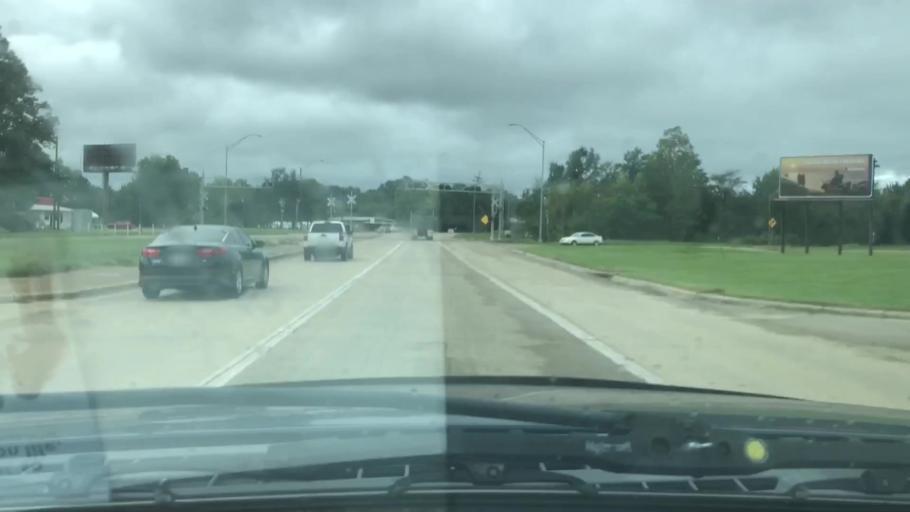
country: US
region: Texas
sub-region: Bowie County
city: Texarkana
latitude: 33.4233
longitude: -94.0702
